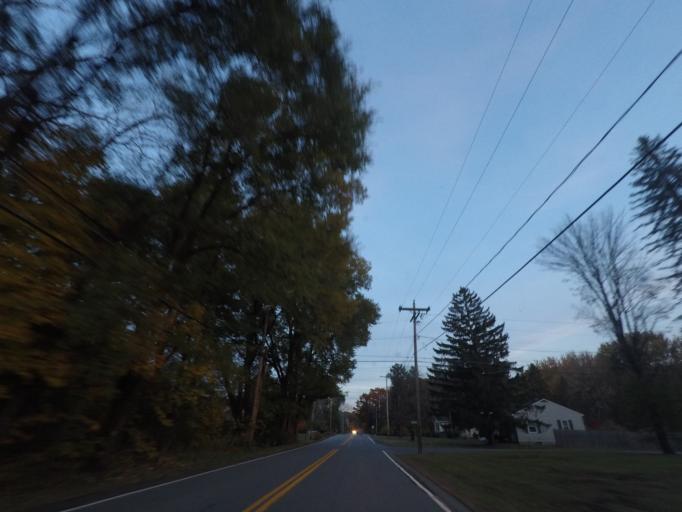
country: US
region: New York
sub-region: Schenectady County
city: Rotterdam
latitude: 42.7520
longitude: -73.9191
